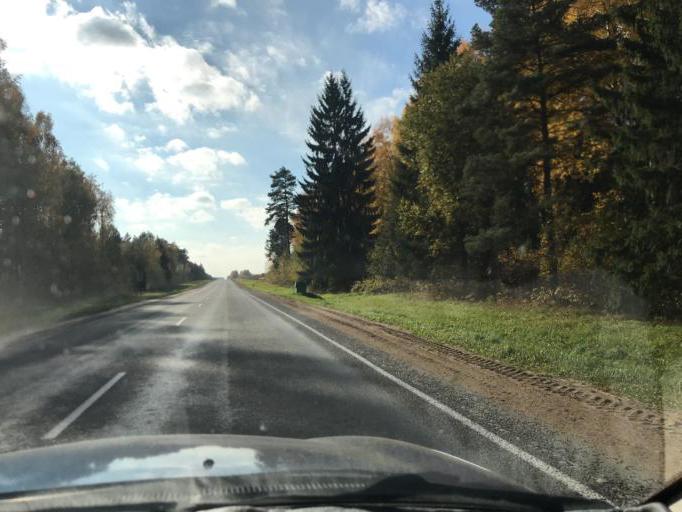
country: BY
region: Grodnenskaya
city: Voranava
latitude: 54.2176
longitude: 25.3540
